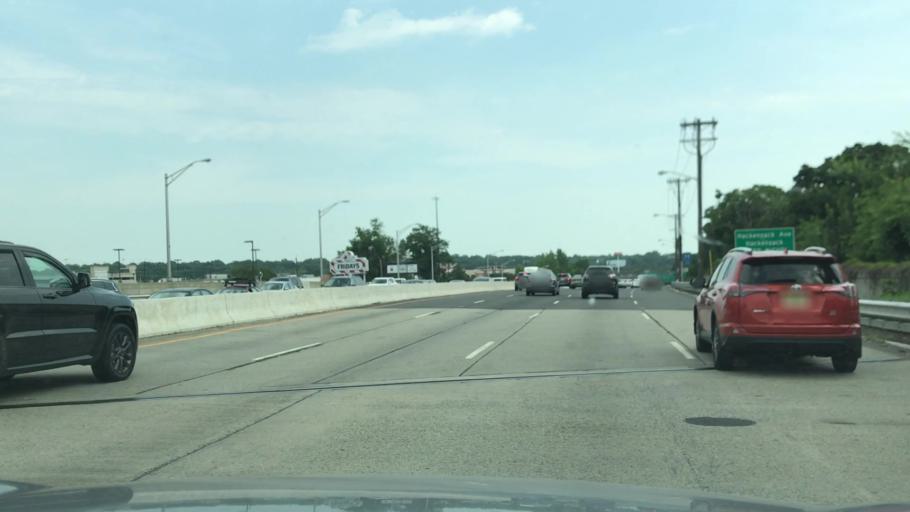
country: US
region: New Jersey
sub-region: Bergen County
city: River Edge
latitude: 40.9086
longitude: -74.0360
